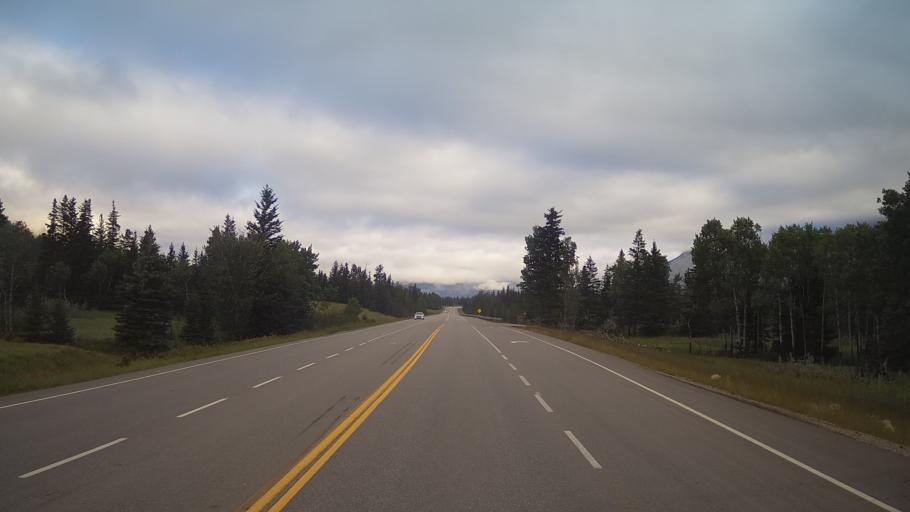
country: CA
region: Alberta
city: Jasper Park Lodge
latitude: 52.9614
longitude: -118.0500
